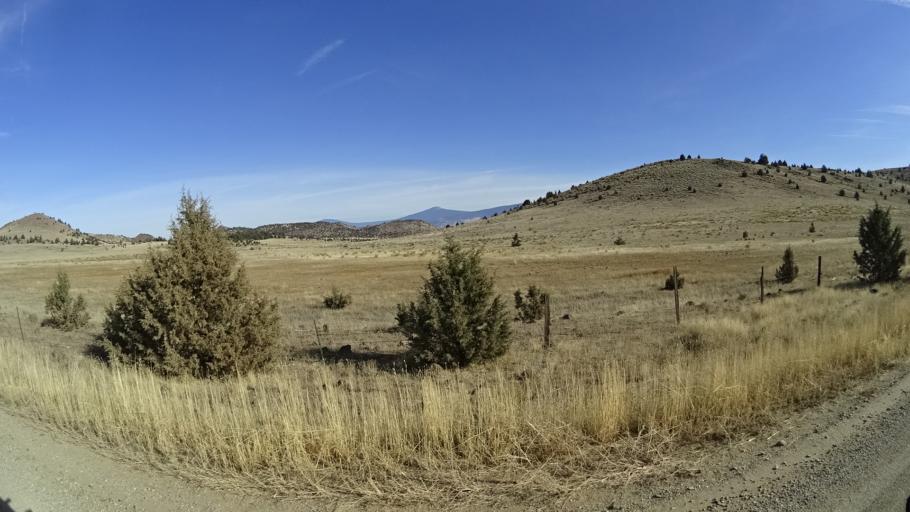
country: US
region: California
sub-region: Siskiyou County
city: Weed
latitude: 41.5476
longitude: -122.4735
